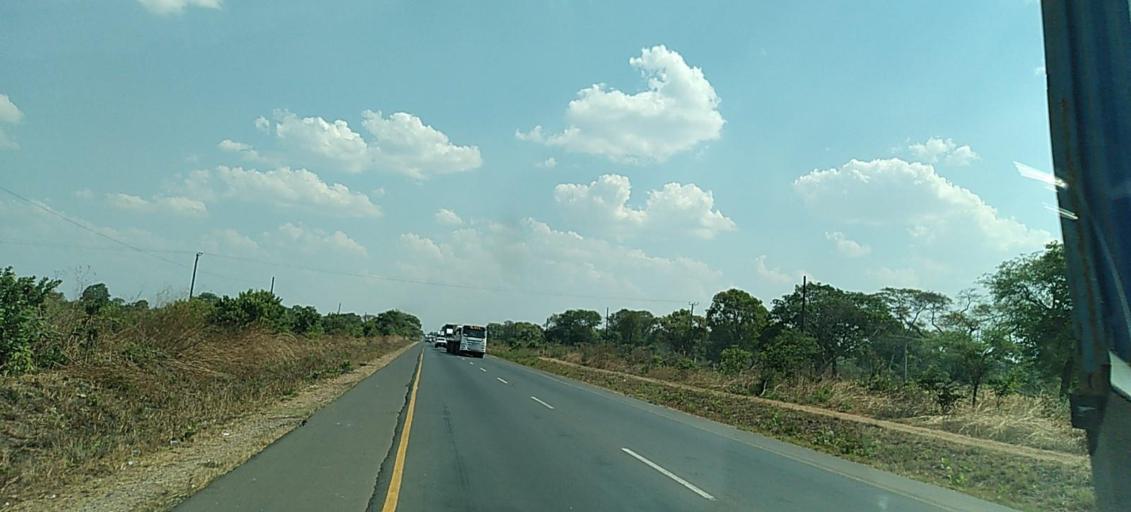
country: ZM
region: Central
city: Chibombo
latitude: -14.8123
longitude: 28.0539
